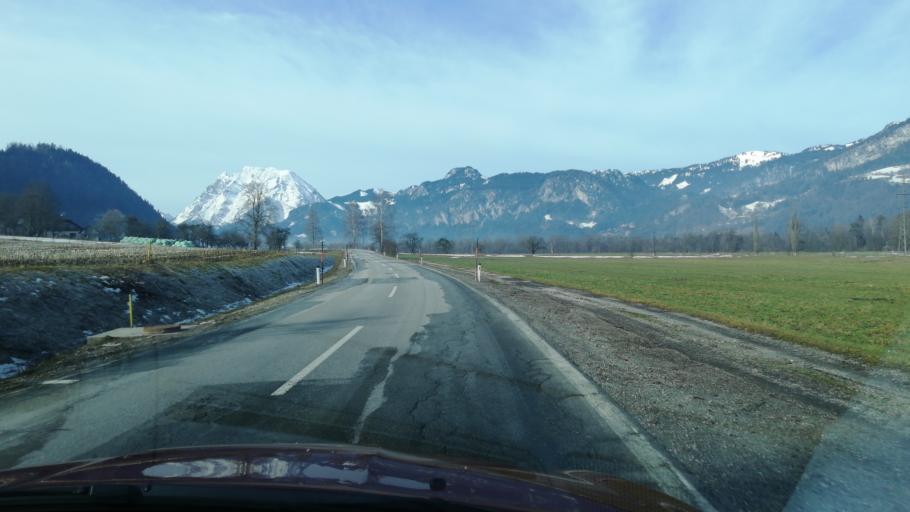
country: AT
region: Styria
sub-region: Politischer Bezirk Liezen
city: Weissenbach bei Liezen
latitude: 47.5465
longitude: 14.1961
